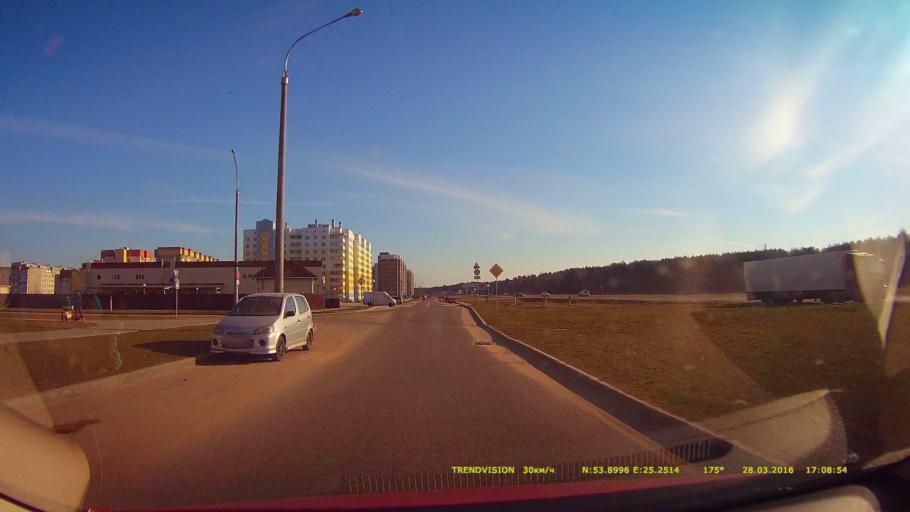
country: BY
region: Grodnenskaya
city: Lida
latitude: 53.8993
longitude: 25.2515
